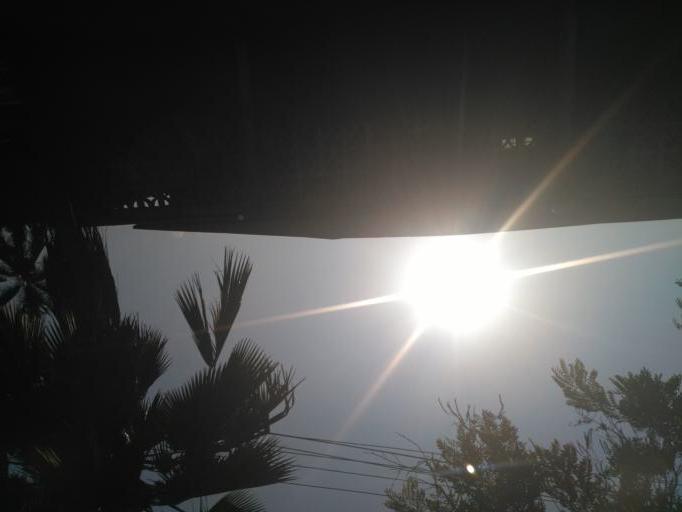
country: TZ
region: Dar es Salaam
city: Dar es Salaam
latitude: -6.9072
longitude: 39.2672
